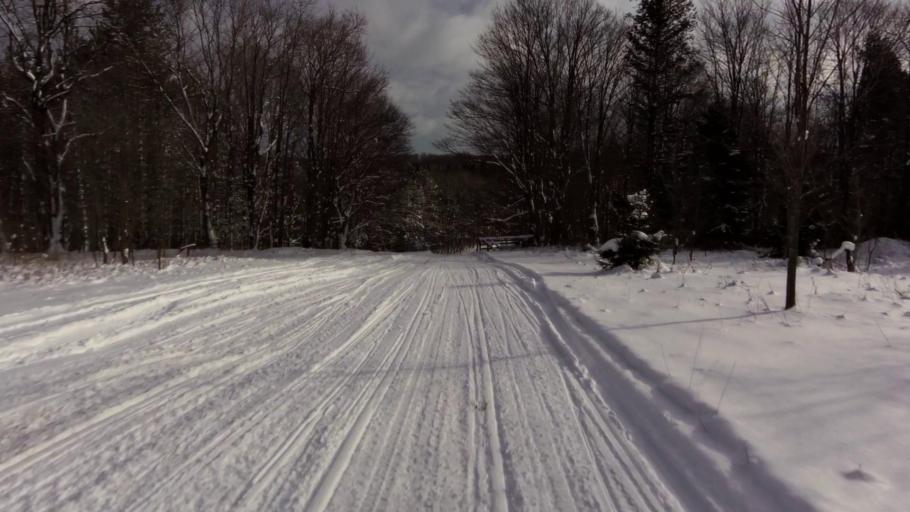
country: US
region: New York
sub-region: Cattaraugus County
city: Franklinville
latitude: 42.2995
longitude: -78.5187
